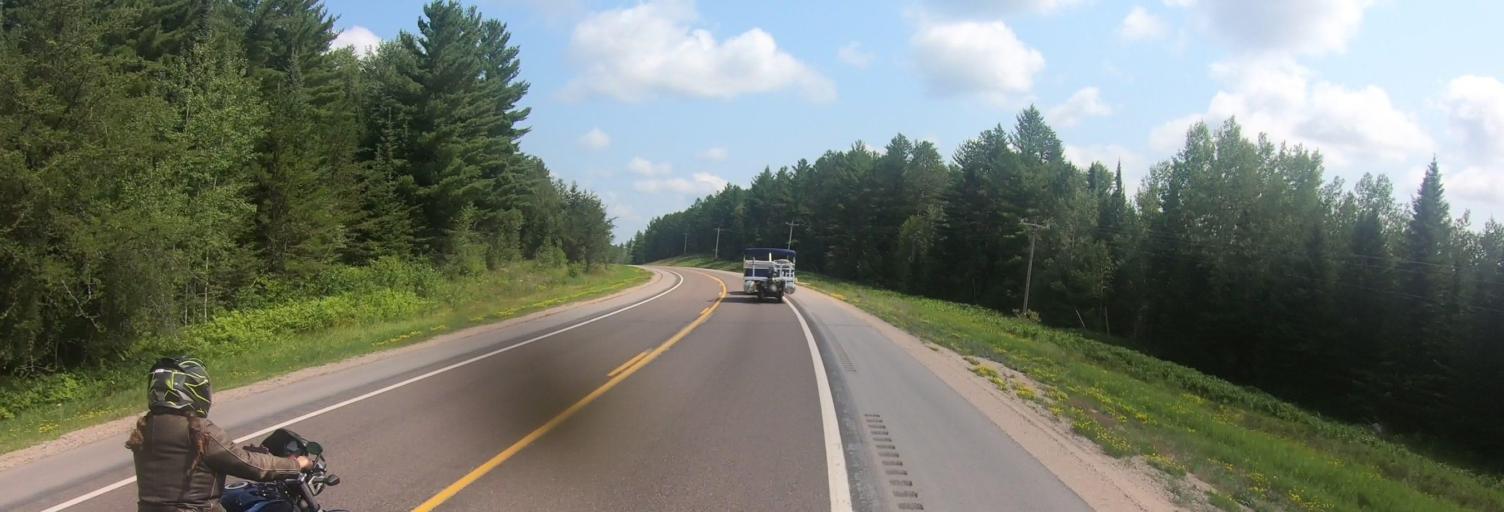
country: US
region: Minnesota
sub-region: Saint Louis County
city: Mountain Iron
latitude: 48.0932
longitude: -92.5937
